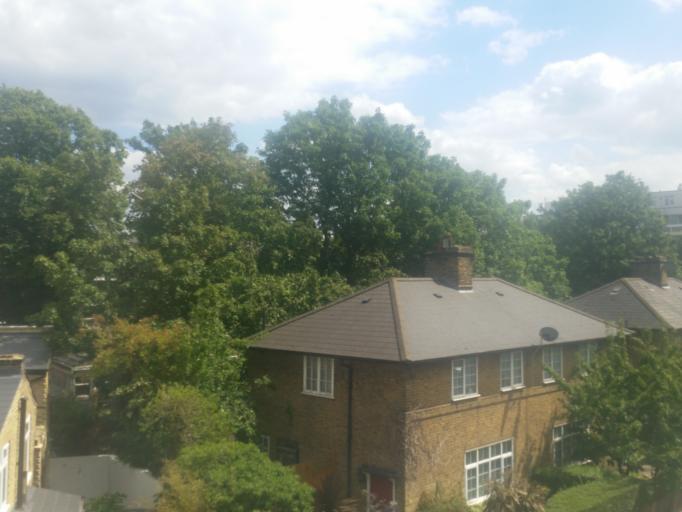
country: GB
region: England
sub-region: Greater London
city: Brixton
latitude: 51.4701
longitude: -0.1014
